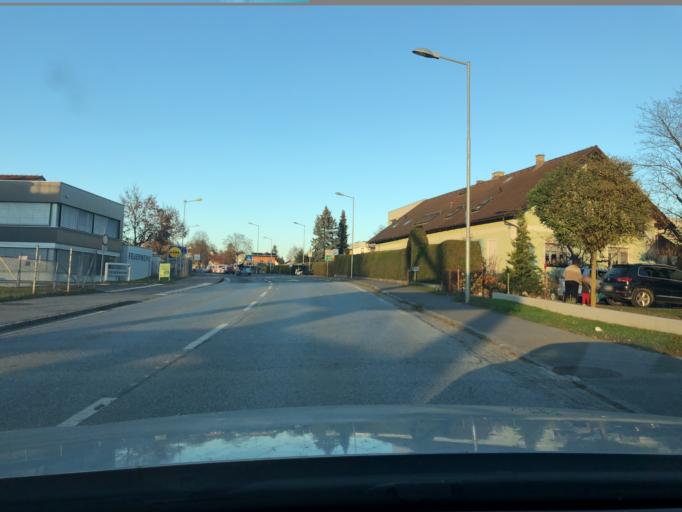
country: AT
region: Styria
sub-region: Politischer Bezirk Weiz
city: Gleisdorf
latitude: 47.1106
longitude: 15.7080
